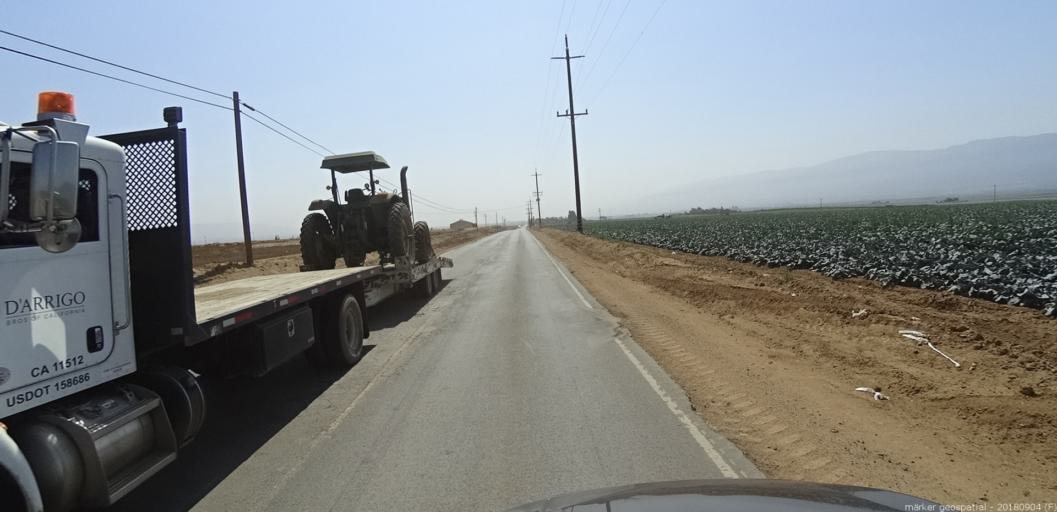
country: US
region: California
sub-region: Monterey County
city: Chualar
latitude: 36.5596
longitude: -121.4804
